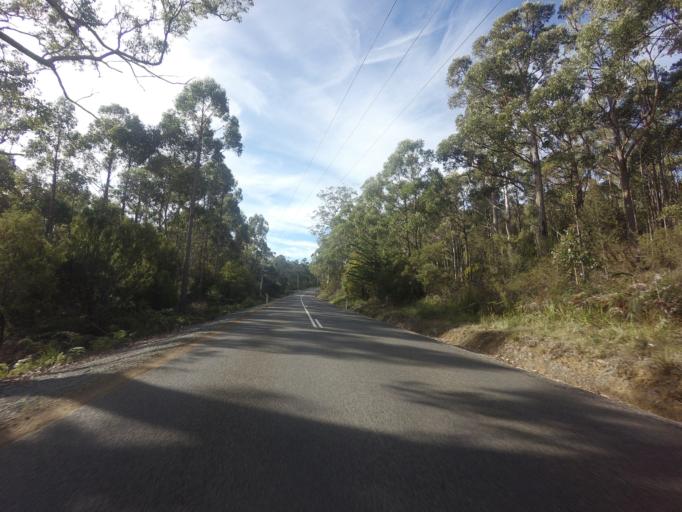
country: AU
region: Tasmania
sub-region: Clarence
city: Sandford
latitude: -43.0605
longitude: 147.8439
